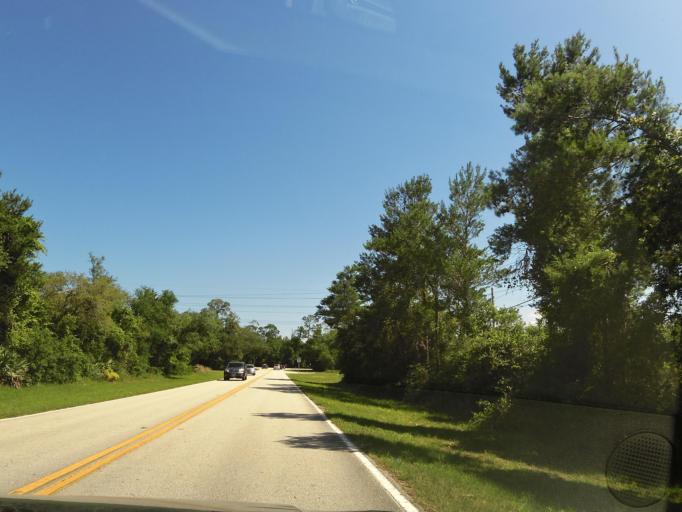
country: US
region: Florida
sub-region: Flagler County
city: Flagler Beach
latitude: 29.4056
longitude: -81.1473
